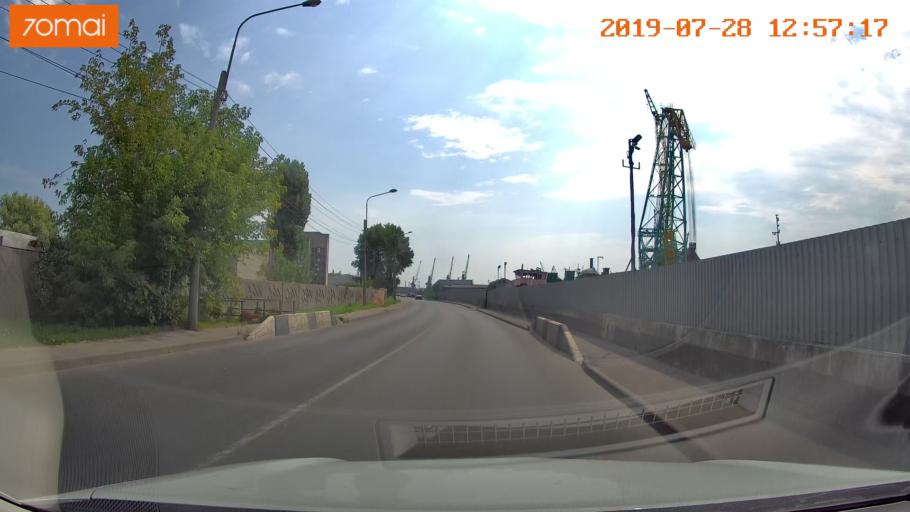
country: RU
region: Kaliningrad
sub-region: Gorod Kaliningrad
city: Kaliningrad
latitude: 54.7074
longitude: 20.4678
